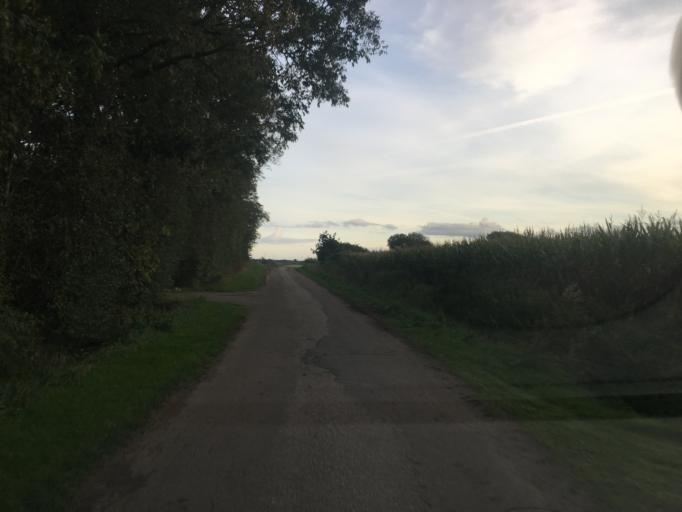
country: DK
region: South Denmark
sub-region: Tonder Kommune
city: Tonder
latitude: 54.9789
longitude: 8.9077
